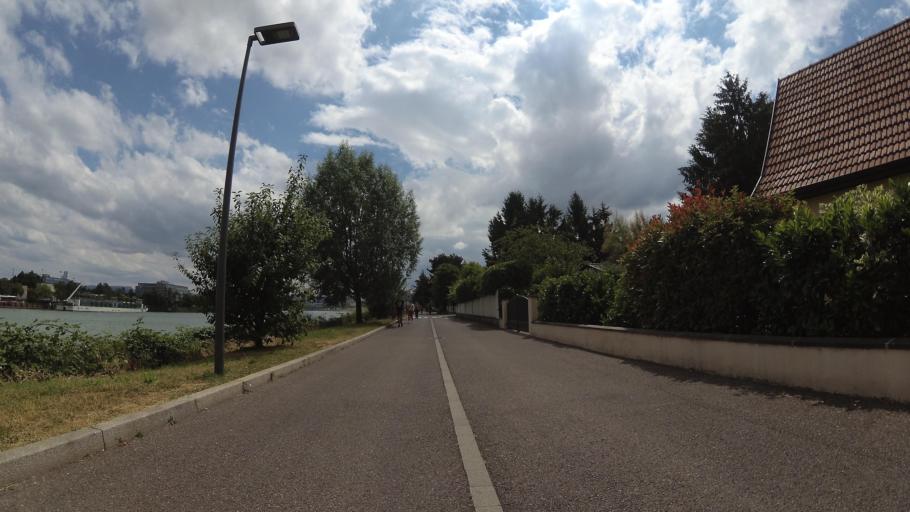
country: FR
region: Alsace
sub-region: Departement du Haut-Rhin
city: Village-Neuf
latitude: 47.5862
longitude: 7.5853
